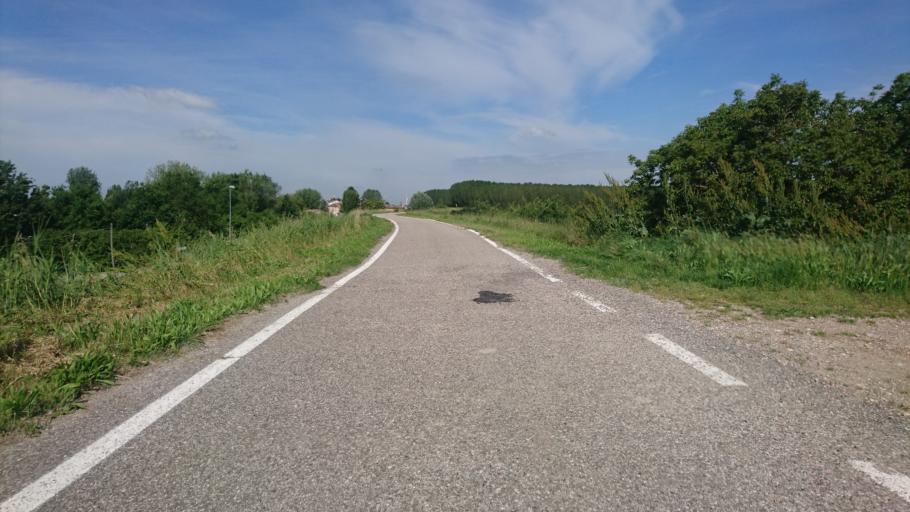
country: IT
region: Lombardy
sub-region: Provincia di Mantova
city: Carbonara di Po
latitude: 45.0377
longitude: 11.2333
